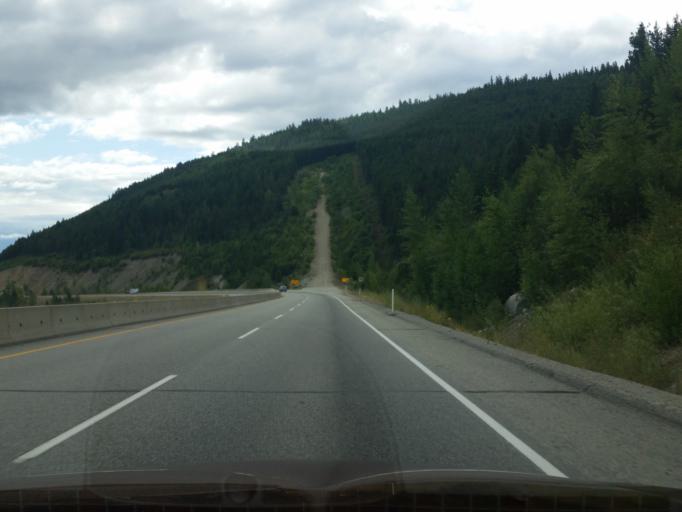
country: CA
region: British Columbia
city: Peachland
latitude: 49.8666
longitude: -119.8722
